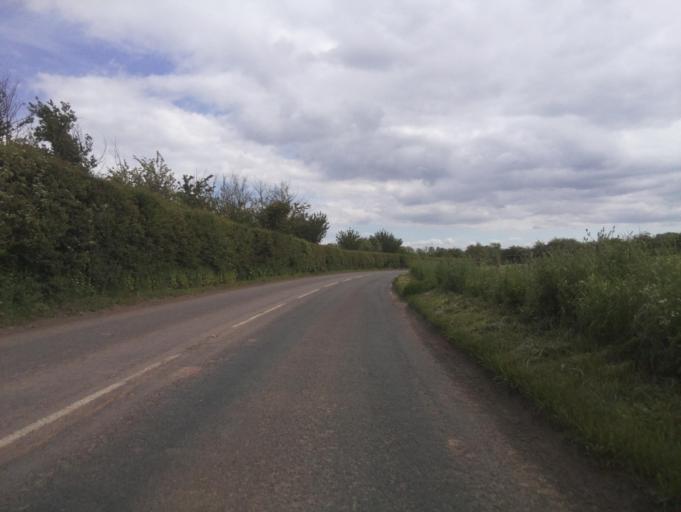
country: GB
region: England
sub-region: Herefordshire
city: Ledbury
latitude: 52.0659
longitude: -2.4465
